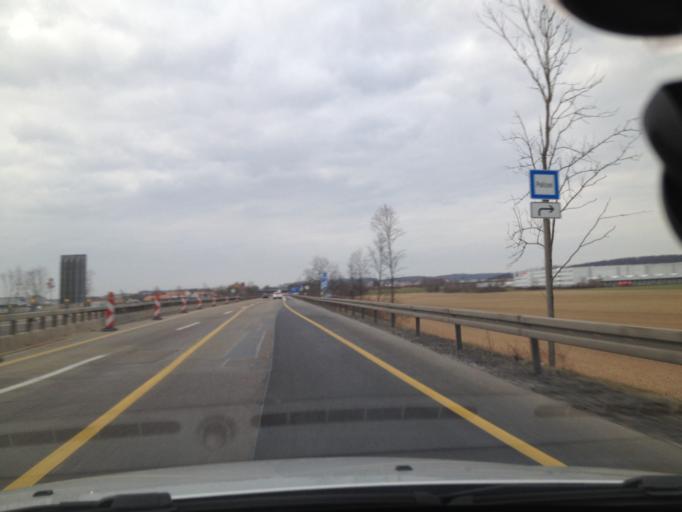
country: DE
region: Hesse
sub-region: Regierungsbezirk Darmstadt
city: Langenselbold
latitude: 50.1735
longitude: 9.0159
